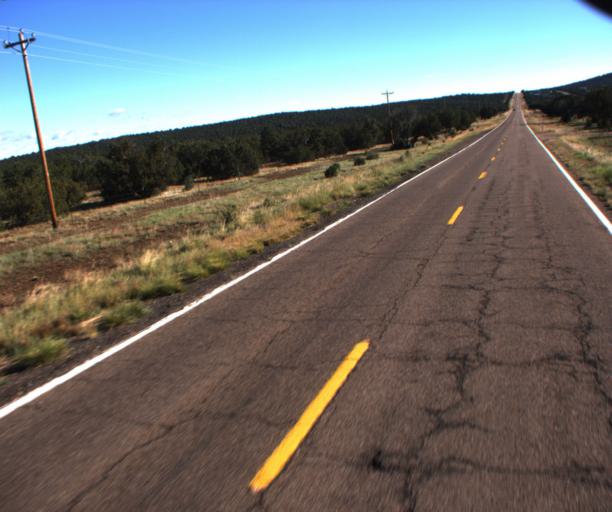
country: US
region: Arizona
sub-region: Navajo County
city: White Mountain Lake
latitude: 34.2981
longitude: -109.7946
